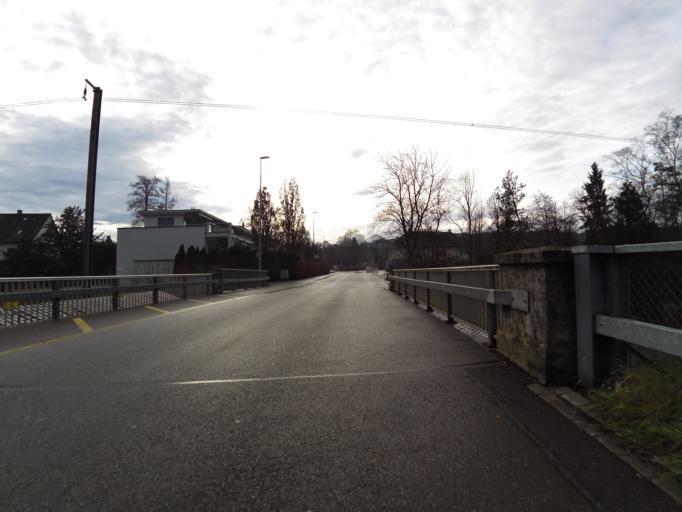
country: CH
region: Thurgau
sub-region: Frauenfeld District
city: Frauenfeld
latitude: 47.5557
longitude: 8.8900
